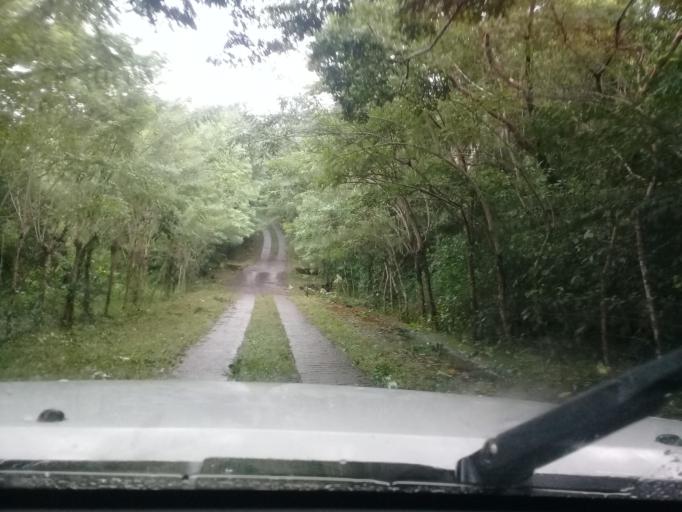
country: MX
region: Veracruz
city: Santiago Tuxtla
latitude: 18.4534
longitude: -95.2931
